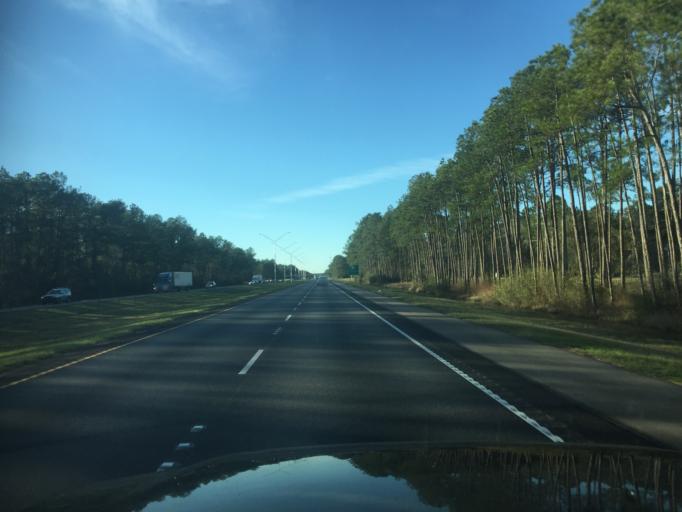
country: US
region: Louisiana
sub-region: Saint Tammany Parish
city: Lacombe
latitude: 30.3486
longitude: -89.9130
